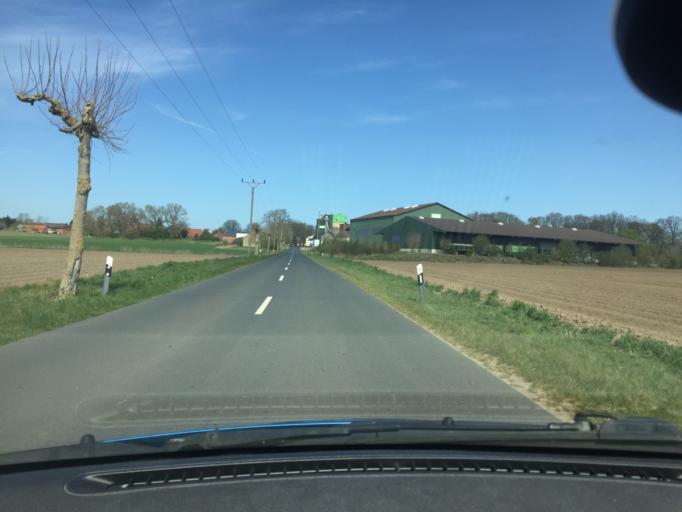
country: DE
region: Lower Saxony
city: Ratzlingen
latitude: 52.9710
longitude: 10.6787
